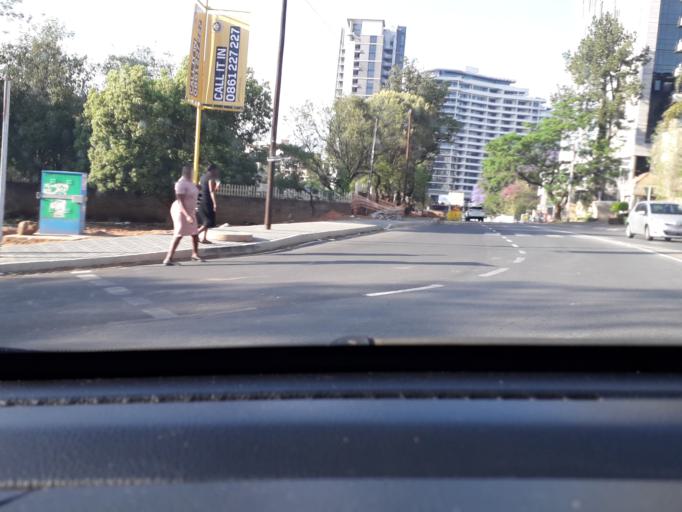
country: ZA
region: Gauteng
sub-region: City of Johannesburg Metropolitan Municipality
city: Johannesburg
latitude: -26.0933
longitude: 28.0545
